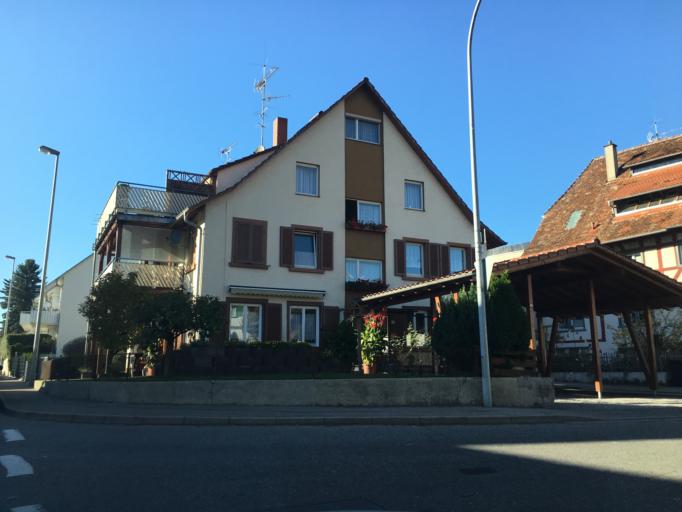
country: CH
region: Thurgau
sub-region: Kreuzlingen District
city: Gottlieben
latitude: 47.6916
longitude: 9.1447
